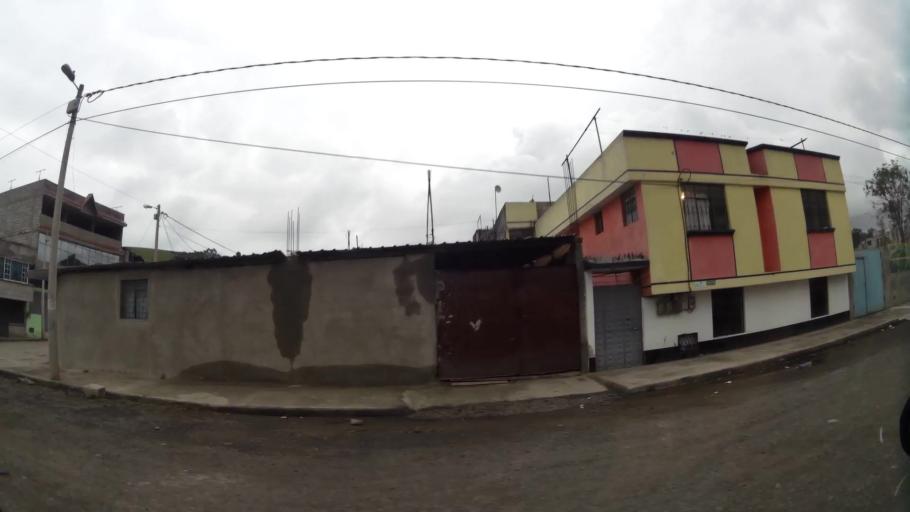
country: EC
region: Pichincha
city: Sangolqui
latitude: -0.3275
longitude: -78.5333
